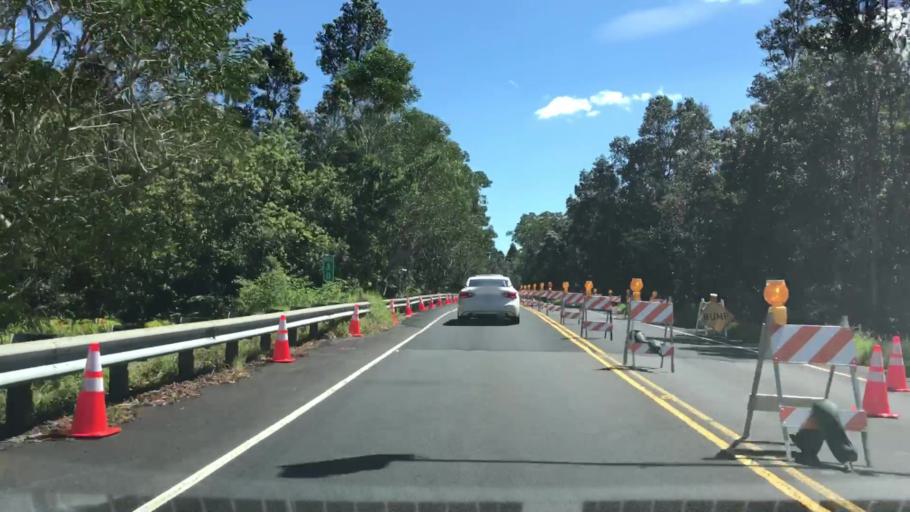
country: US
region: Hawaii
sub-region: Hawaii County
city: Volcano
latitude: 19.4355
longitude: -155.2748
